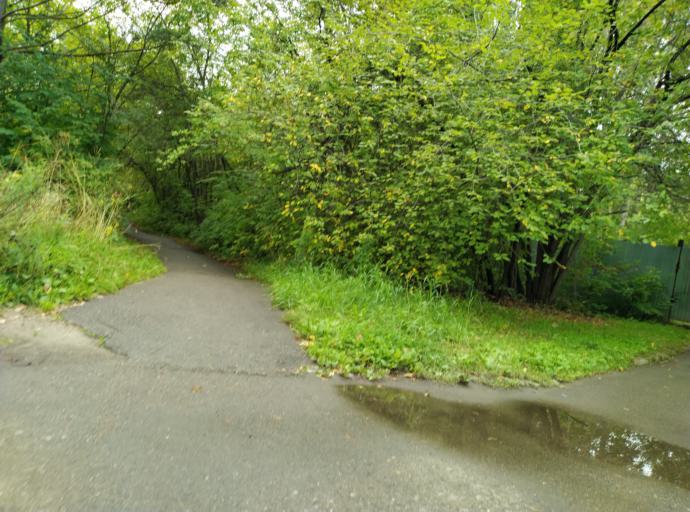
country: RU
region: Krasnoyarskiy
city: Krasnoyarsk
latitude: 55.9886
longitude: 92.7619
